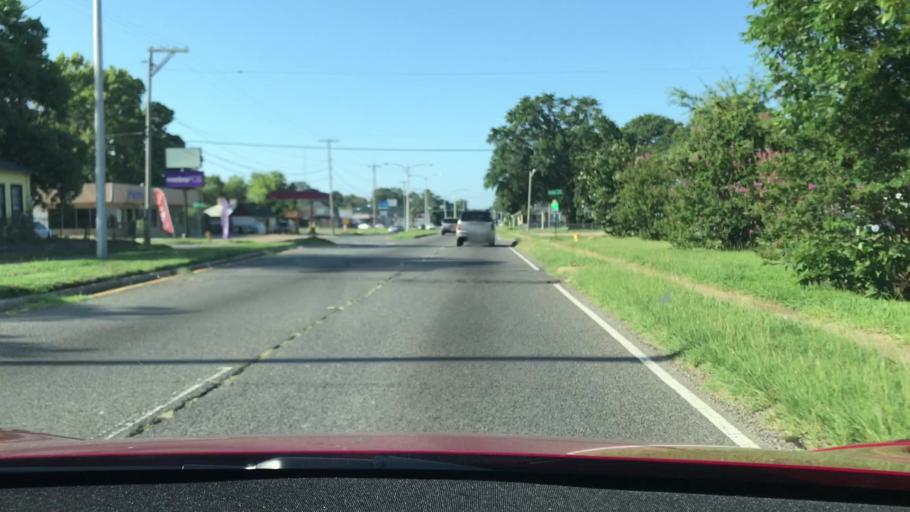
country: US
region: Louisiana
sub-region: Caddo Parish
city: Shreveport
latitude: 32.4741
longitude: -93.7801
